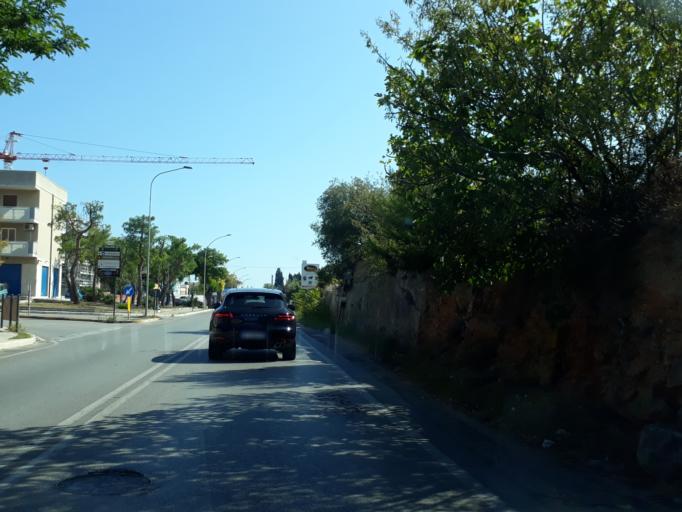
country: IT
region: Apulia
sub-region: Provincia di Bari
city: Monopoli
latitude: 40.9456
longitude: 17.2957
